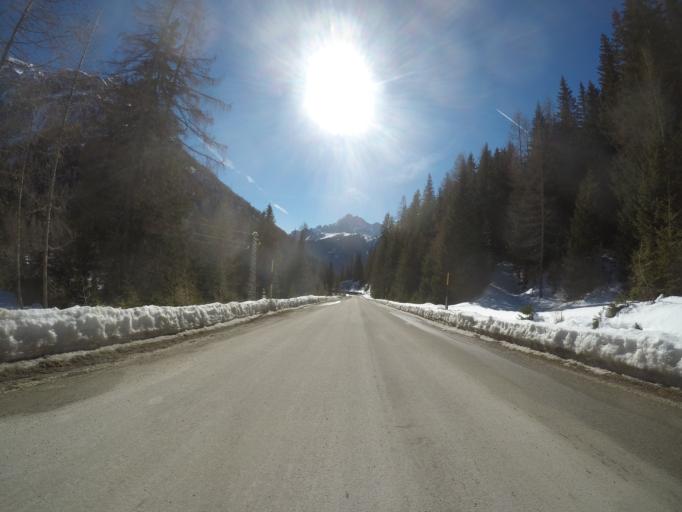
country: IT
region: Veneto
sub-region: Provincia di Belluno
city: Colle Santa Lucia
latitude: 46.4742
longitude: 12.0308
